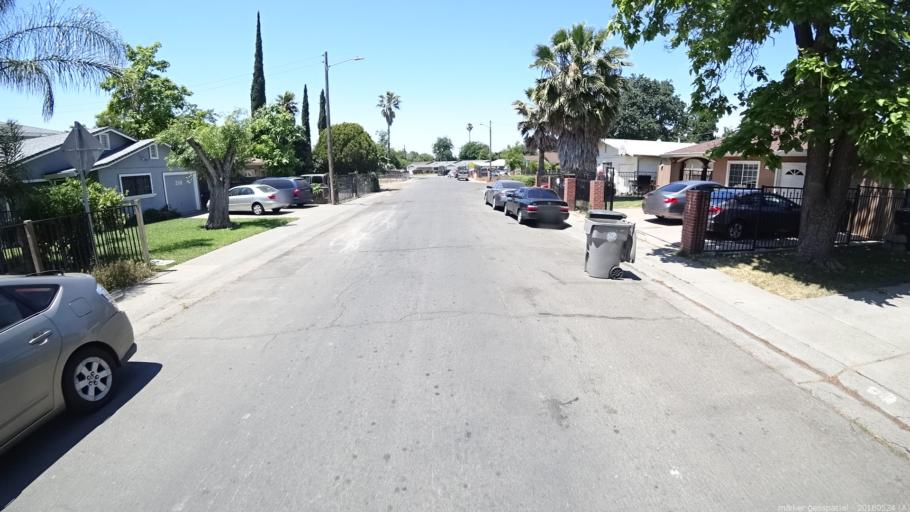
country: US
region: California
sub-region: Sacramento County
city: Sacramento
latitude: 38.6197
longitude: -121.4620
